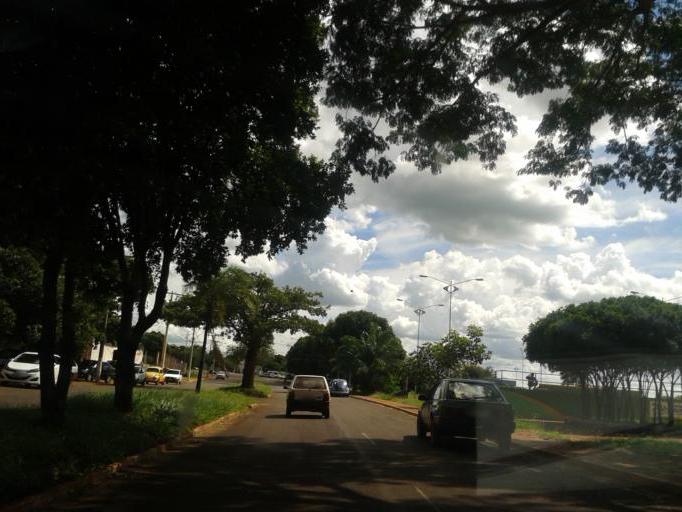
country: BR
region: Minas Gerais
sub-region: Santa Vitoria
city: Santa Vitoria
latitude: -18.8440
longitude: -50.1297
